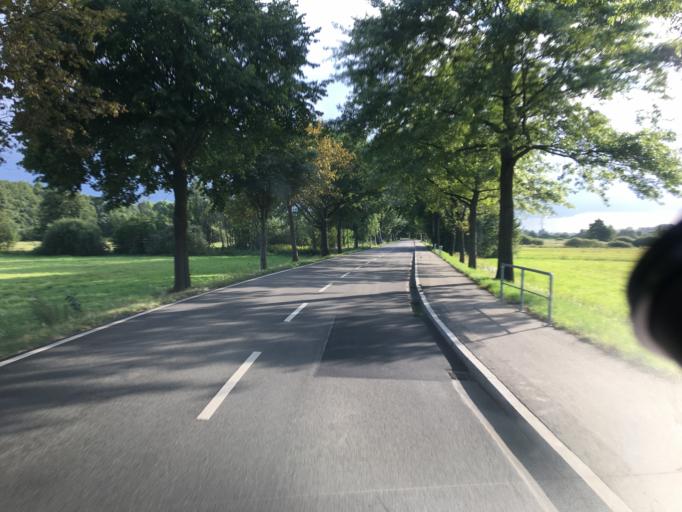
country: DE
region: Lower Saxony
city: Neu Wulmstorf
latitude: 53.4916
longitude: 9.8739
